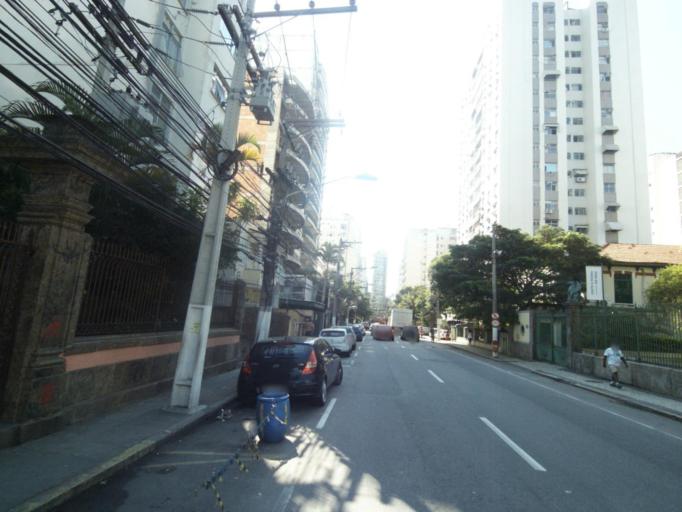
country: BR
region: Rio de Janeiro
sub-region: Niteroi
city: Niteroi
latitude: -22.9034
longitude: -43.1253
